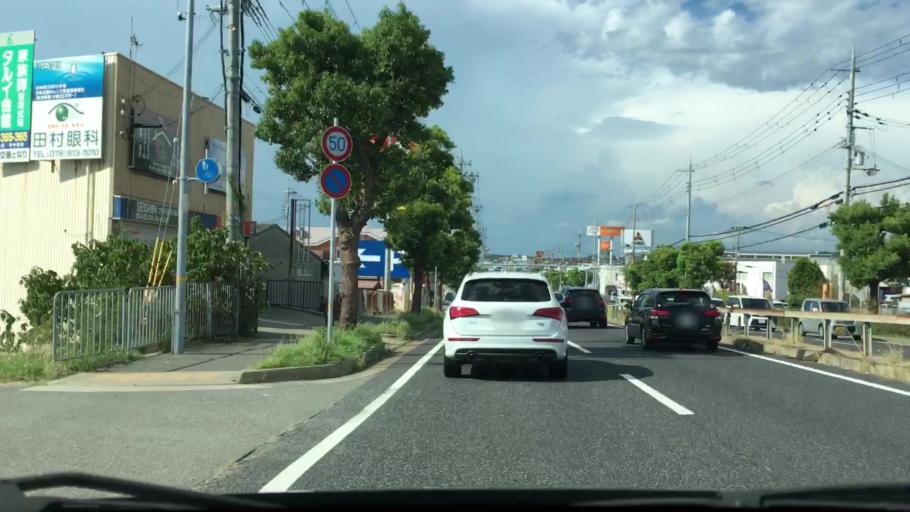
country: JP
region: Hyogo
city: Akashi
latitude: 34.6785
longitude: 134.9820
